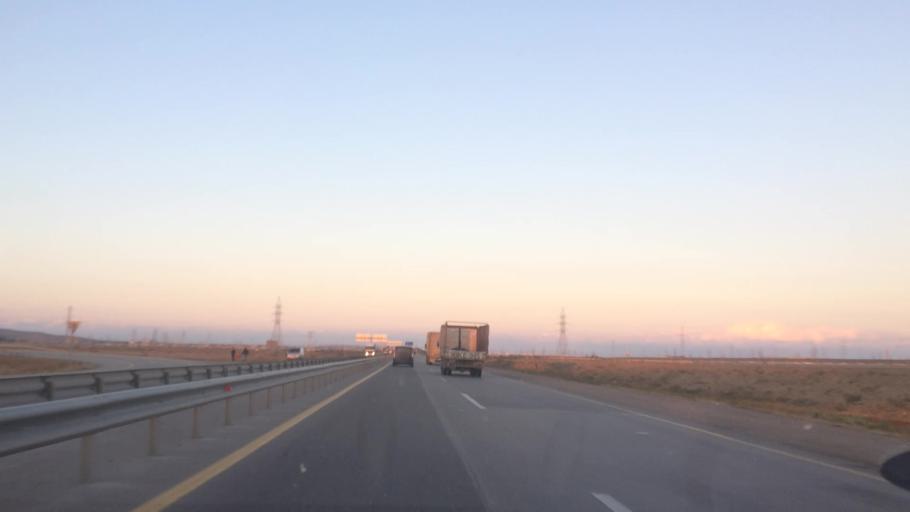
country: AZ
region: Baki
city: Qobustan
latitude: 39.9547
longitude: 49.3803
